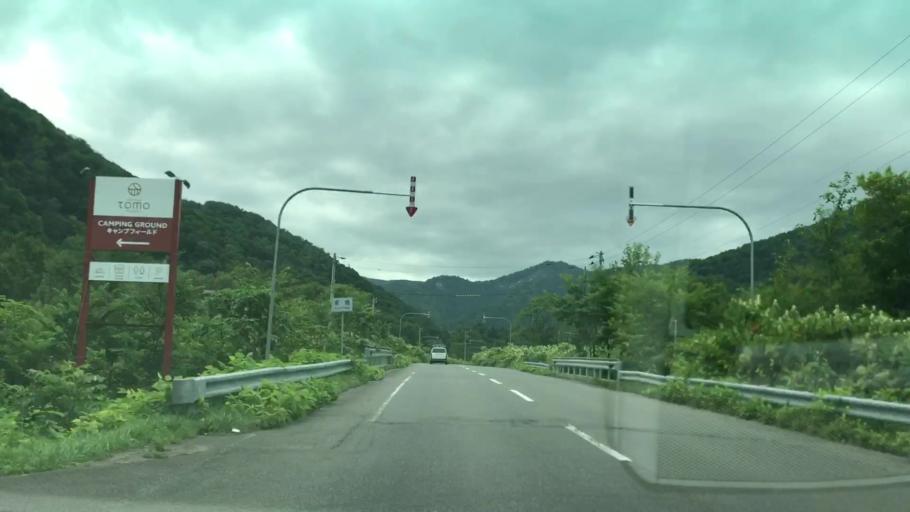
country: JP
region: Hokkaido
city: Yoichi
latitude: 43.0278
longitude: 140.8662
